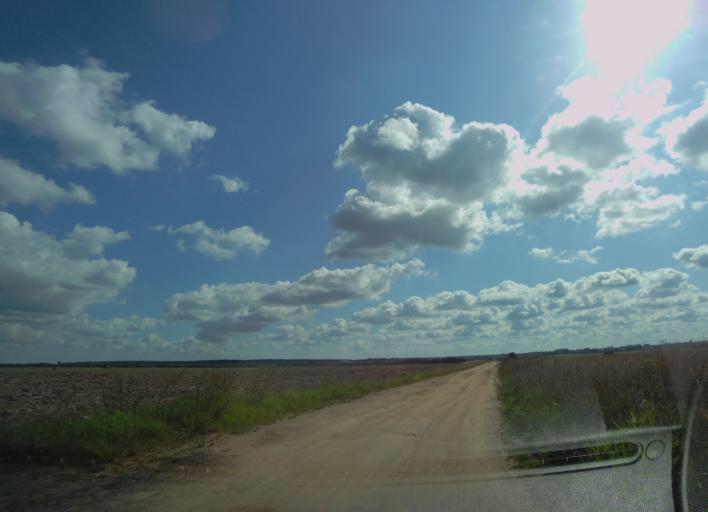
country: BY
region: Minsk
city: Zyembin
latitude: 54.3804
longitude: 28.3462
